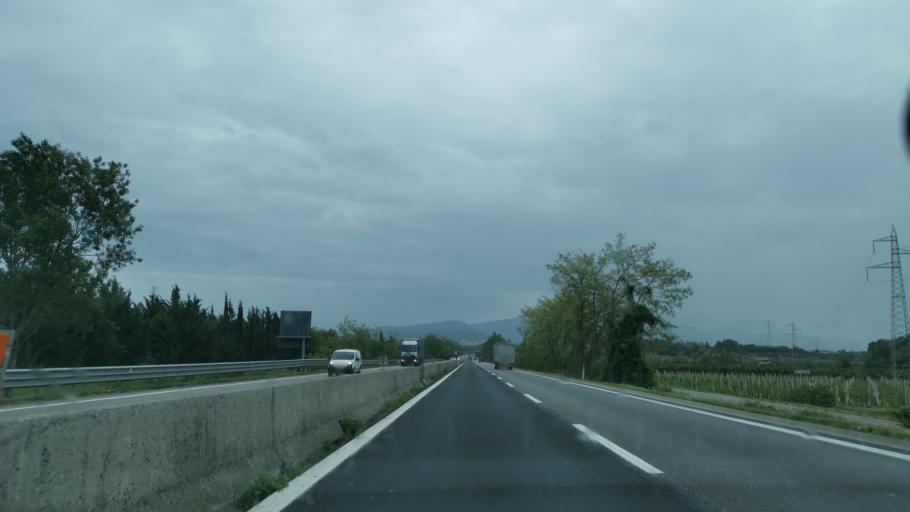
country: IT
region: Veneto
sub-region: Provincia di Verona
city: Calmasino
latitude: 45.4960
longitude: 10.7685
